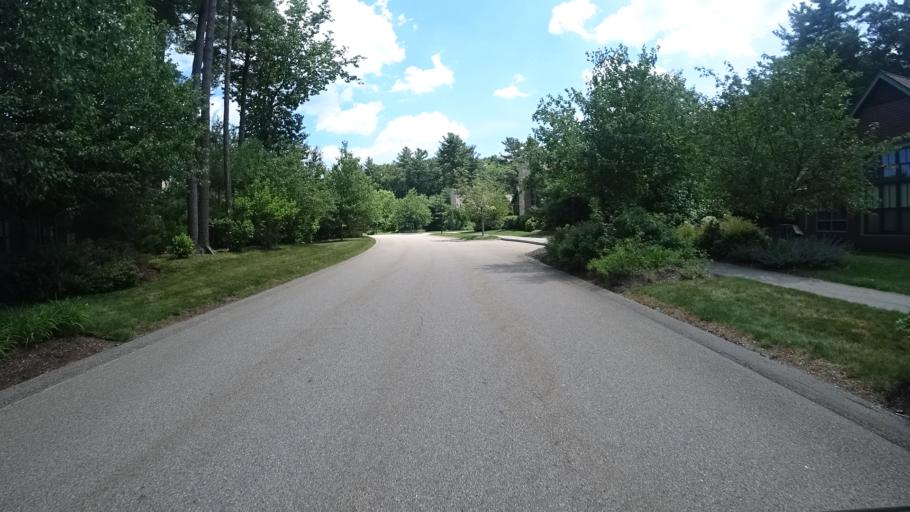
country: US
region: Massachusetts
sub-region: Norfolk County
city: Needham
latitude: 42.2653
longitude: -71.2006
